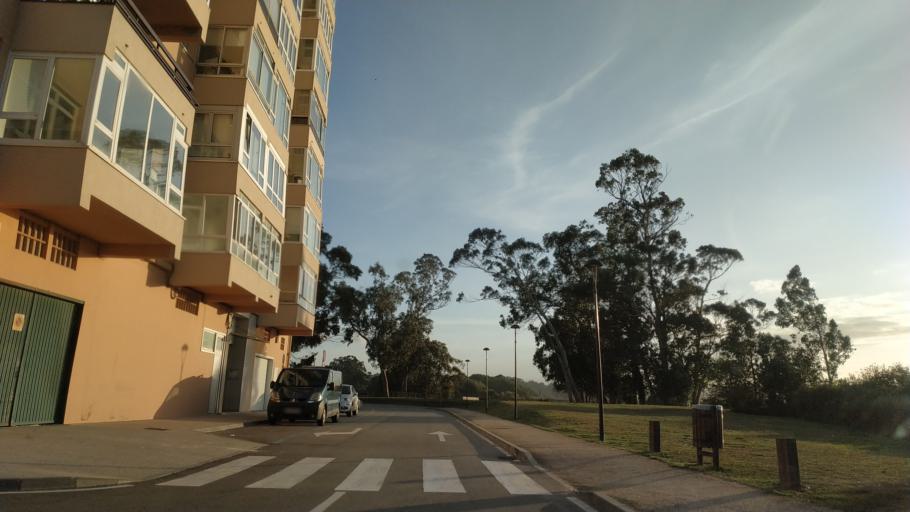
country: ES
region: Galicia
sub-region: Provincia da Coruna
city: Oleiros
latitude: 43.3518
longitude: -8.3474
